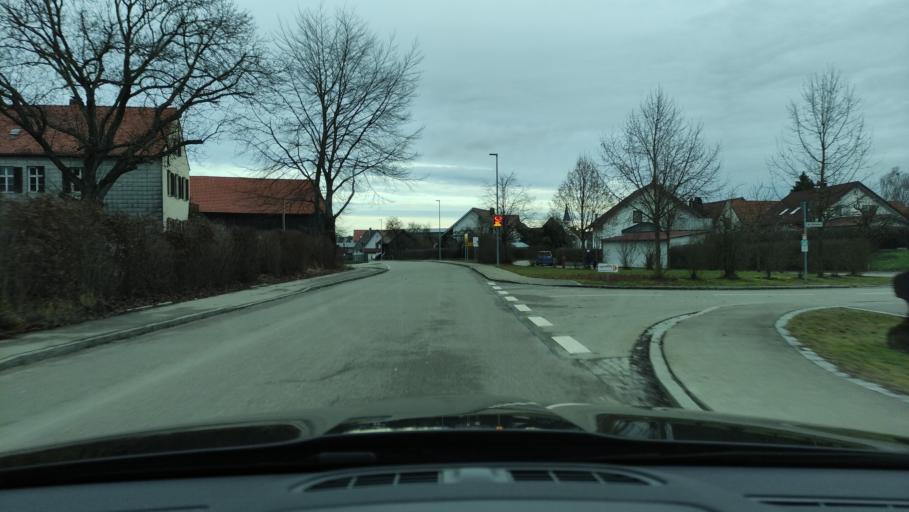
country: DE
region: Bavaria
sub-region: Swabia
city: Breitenthal
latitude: 48.2372
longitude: 10.2914
